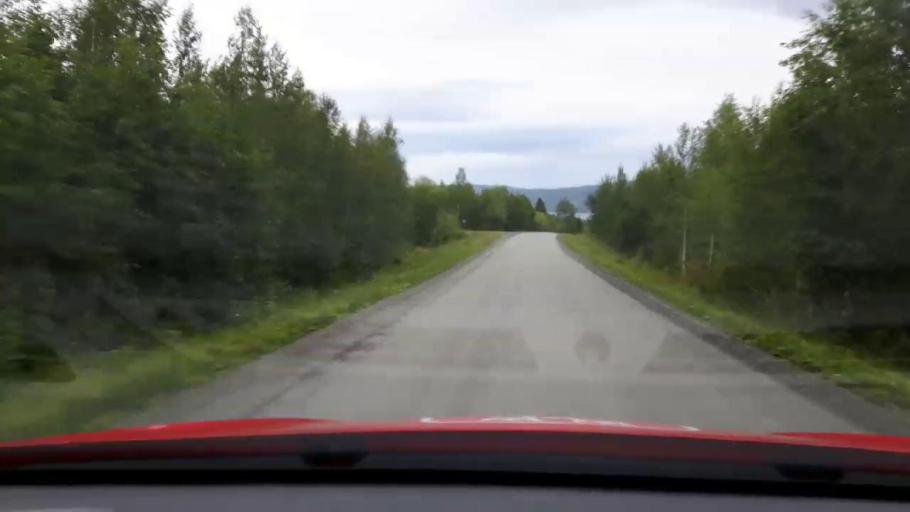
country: SE
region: Jaemtland
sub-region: Are Kommun
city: Are
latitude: 63.4345
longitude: 13.2116
